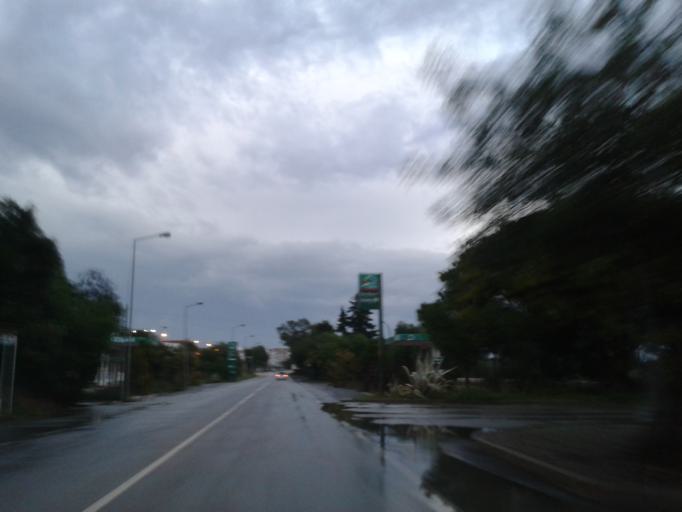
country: PT
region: Faro
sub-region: Lagoa
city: Lagoa
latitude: 37.1363
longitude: -8.4671
